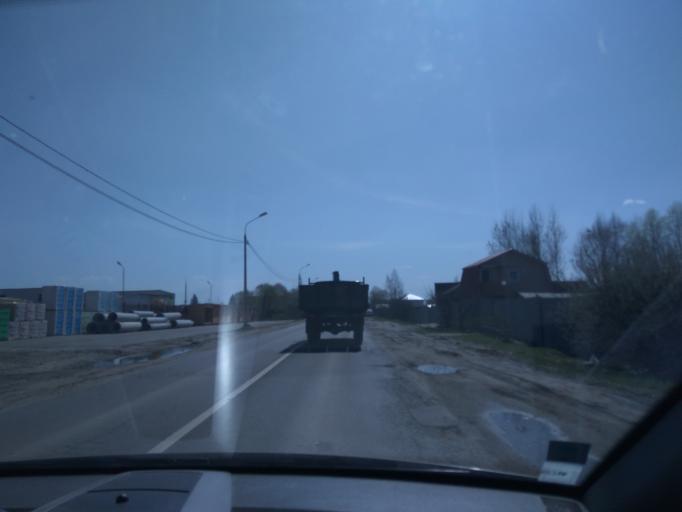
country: RU
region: Moskovskaya
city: Ramenskoye
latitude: 55.5868
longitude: 38.2526
